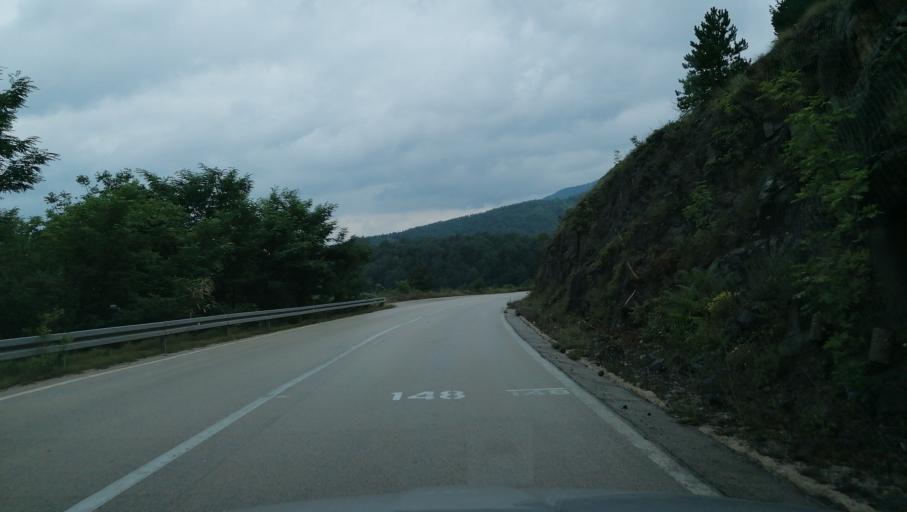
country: RS
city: Durici
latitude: 43.8102
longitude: 19.5147
